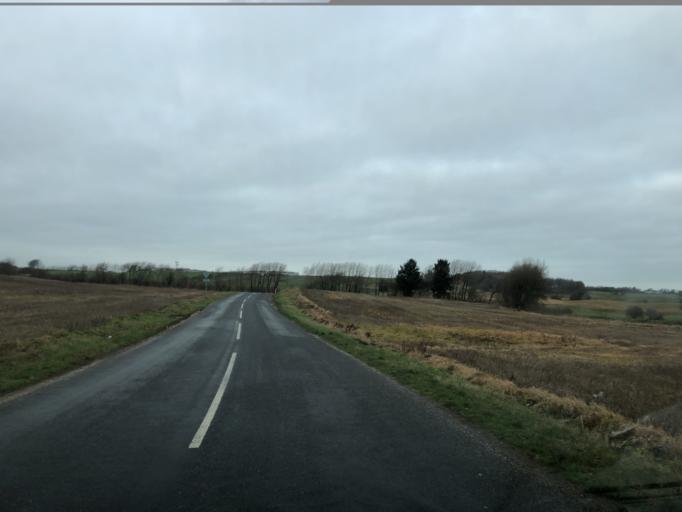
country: DK
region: Central Jutland
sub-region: Viborg Kommune
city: Stoholm
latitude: 56.4327
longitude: 9.1086
